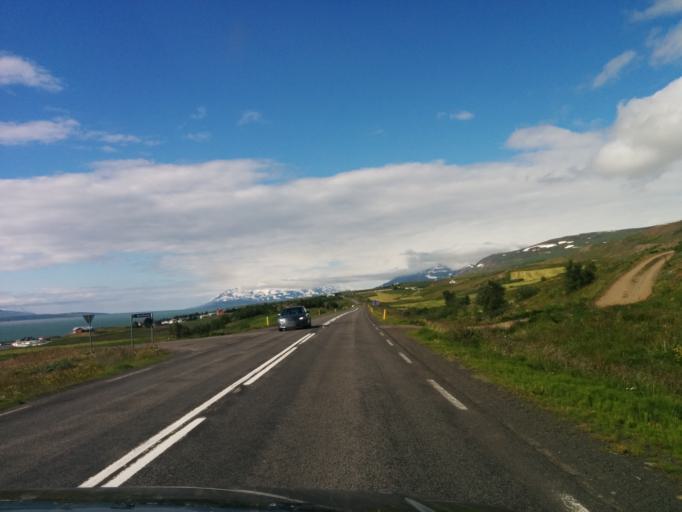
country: IS
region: Northeast
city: Akureyri
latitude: 65.7331
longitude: -18.0739
